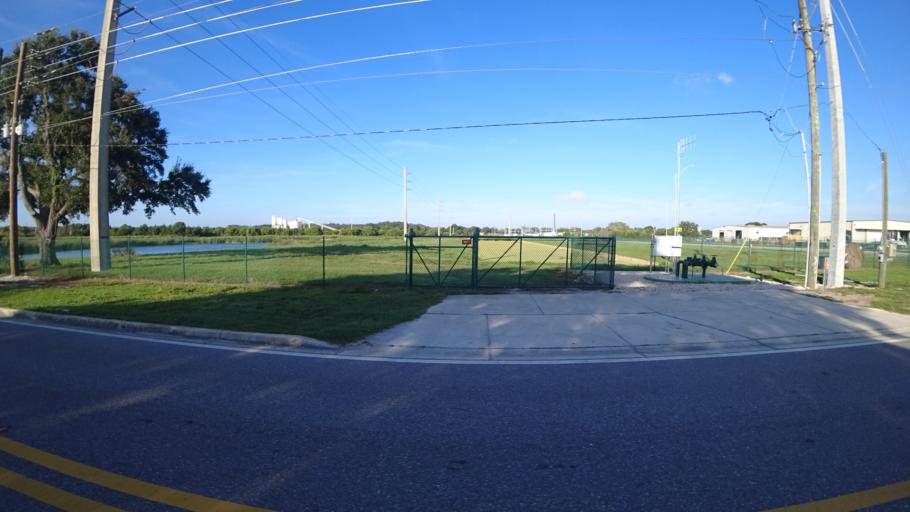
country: US
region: Florida
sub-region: Manatee County
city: Samoset
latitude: 27.4617
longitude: -82.5425
